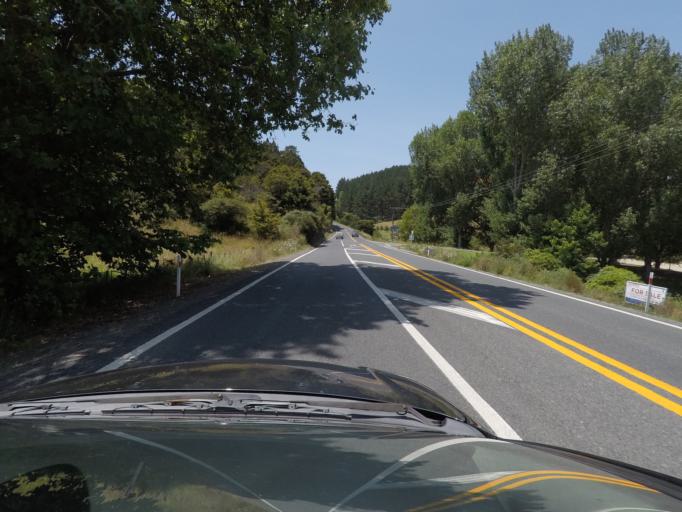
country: NZ
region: Auckland
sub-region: Auckland
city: Warkworth
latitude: -36.3505
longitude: 174.7204
